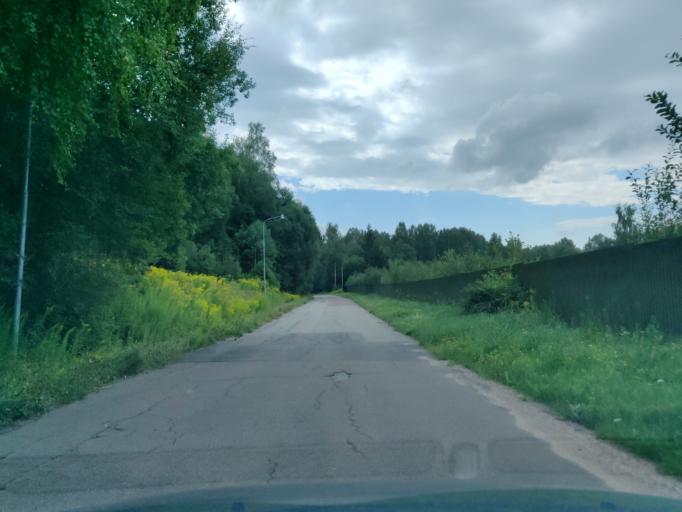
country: SE
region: Vaermland
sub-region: Munkfors Kommun
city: Munkfors
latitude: 59.8533
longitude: 13.5594
